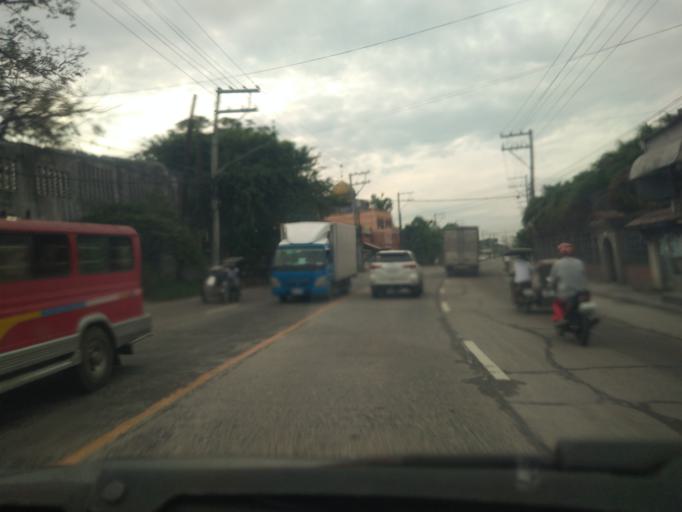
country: PH
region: Central Luzon
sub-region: Province of Pampanga
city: Del Pilar
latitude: 15.0318
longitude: 120.6964
